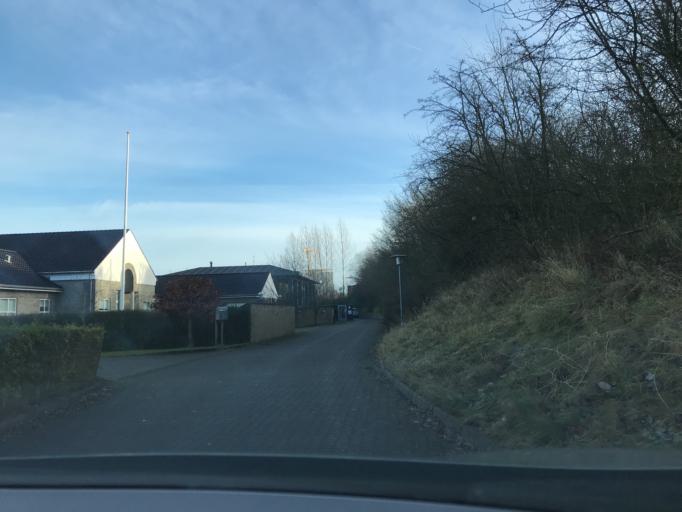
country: DK
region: South Denmark
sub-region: Sonderborg Kommune
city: Dybbol
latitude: 54.9147
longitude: 9.7717
